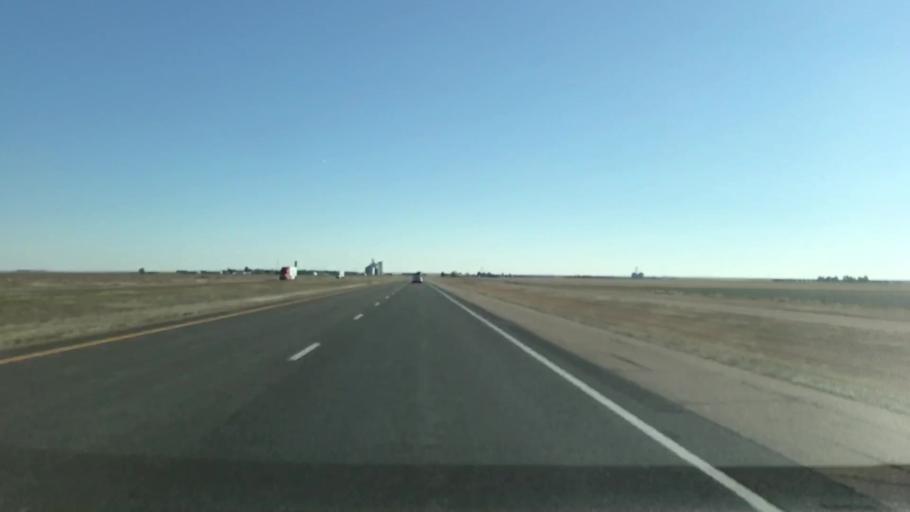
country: US
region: Colorado
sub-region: Lincoln County
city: Hugo
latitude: 39.2819
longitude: -103.3086
